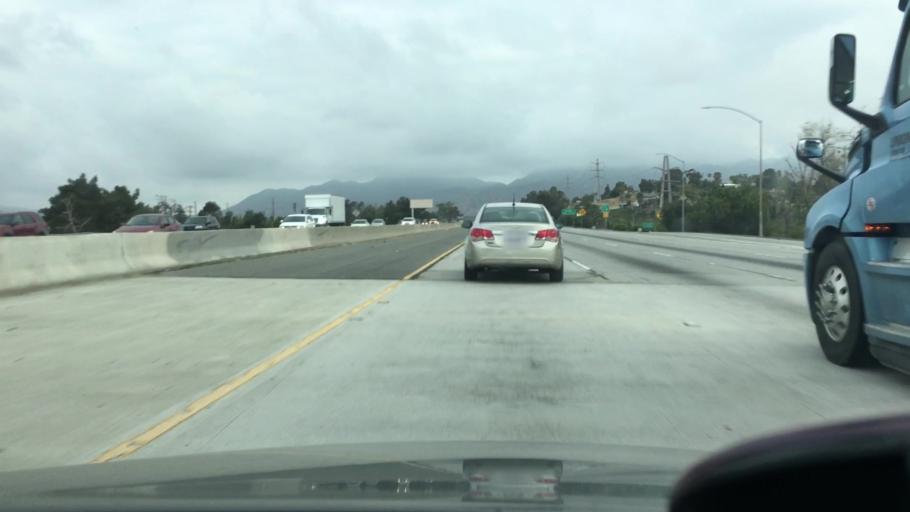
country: US
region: California
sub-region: Los Angeles County
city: San Fernando
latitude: 34.2972
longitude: -118.4171
